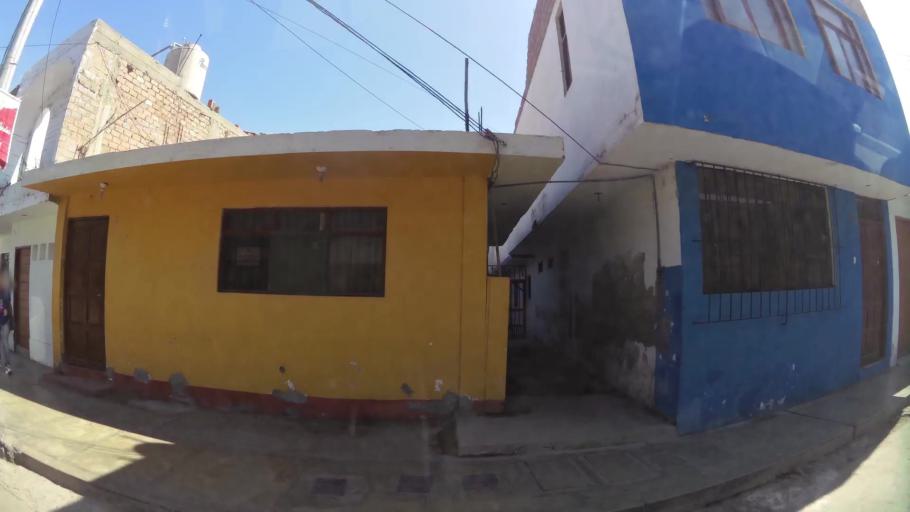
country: PE
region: Lima
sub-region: Provincia de Canete
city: San Vicente de Canete
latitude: -13.0259
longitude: -76.4795
